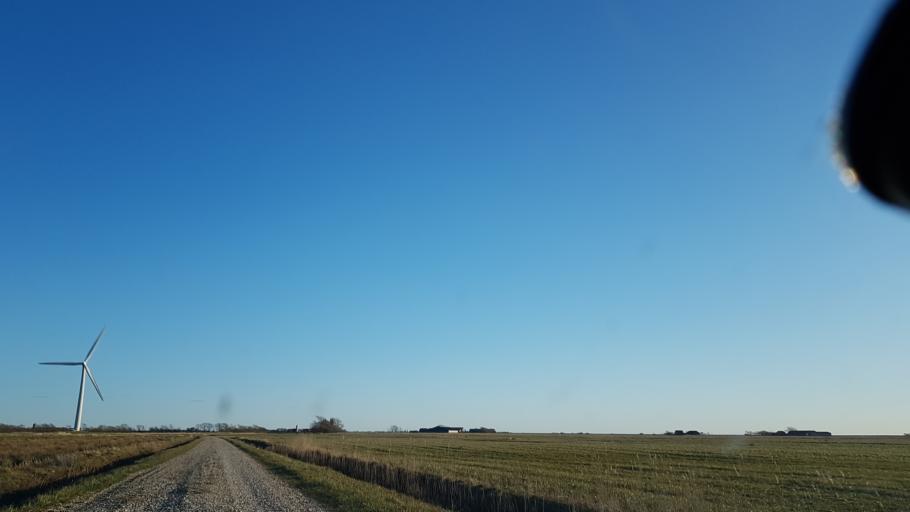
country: DK
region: South Denmark
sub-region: Esbjerg Kommune
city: Bramming
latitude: 55.4106
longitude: 8.6746
